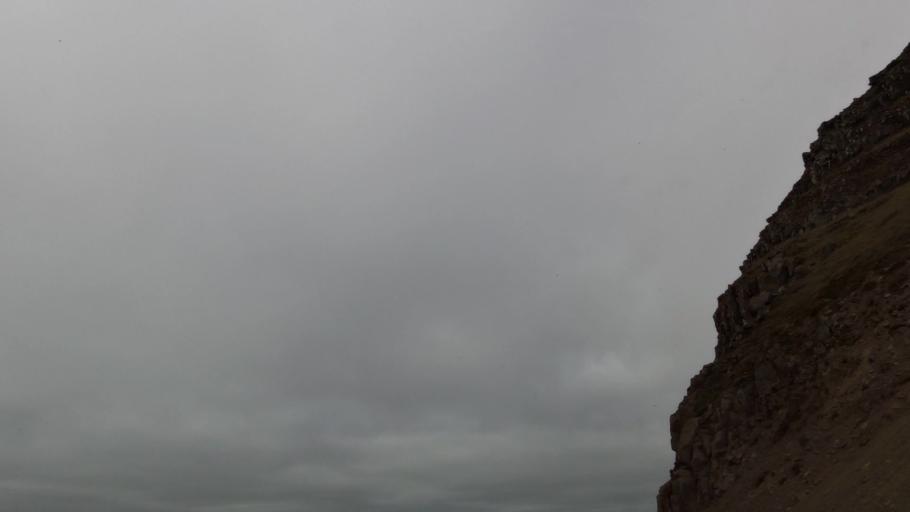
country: IS
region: West
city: Olafsvik
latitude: 65.5102
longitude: -24.5102
